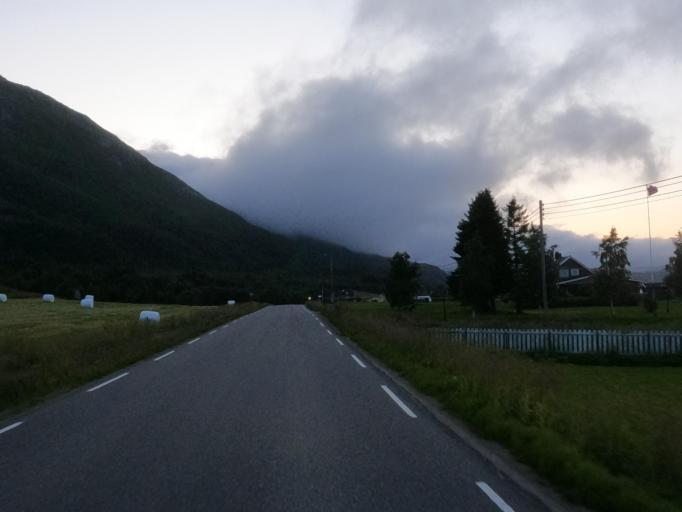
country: NO
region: Nordland
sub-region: Lodingen
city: Lodingen
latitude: 68.5688
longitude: 15.7981
